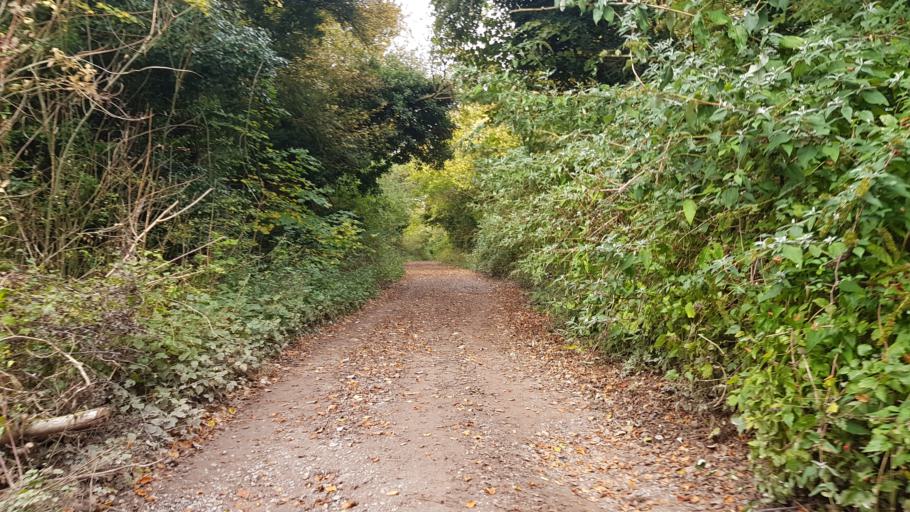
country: GB
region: England
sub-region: Surrey
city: Guildford
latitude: 51.2287
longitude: -0.6131
